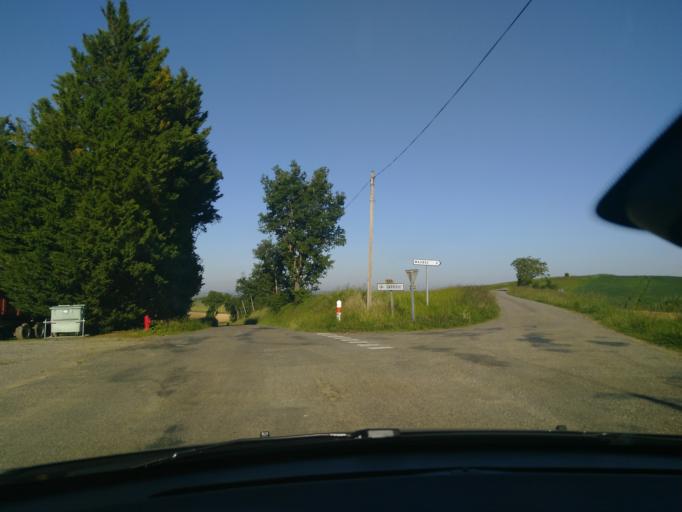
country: FR
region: Midi-Pyrenees
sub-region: Departement du Tarn-et-Garonne
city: Beaumont-de-Lomagne
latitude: 43.7835
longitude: 0.9688
